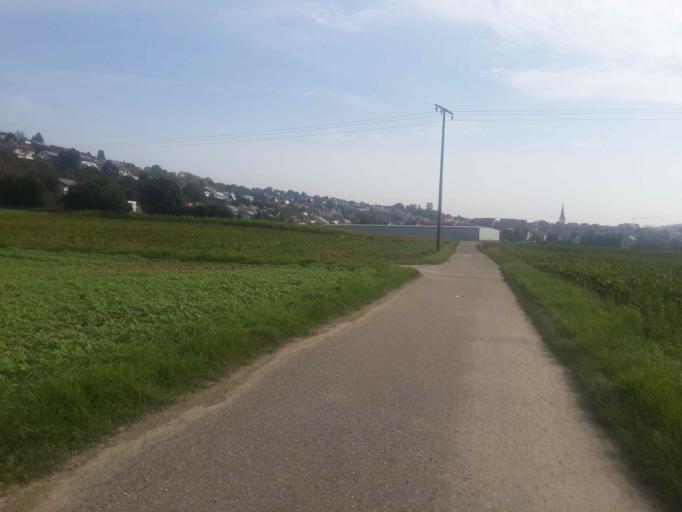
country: DE
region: Baden-Wuerttemberg
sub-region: Regierungsbezirk Stuttgart
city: Neudenau
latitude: 49.2924
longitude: 9.2599
